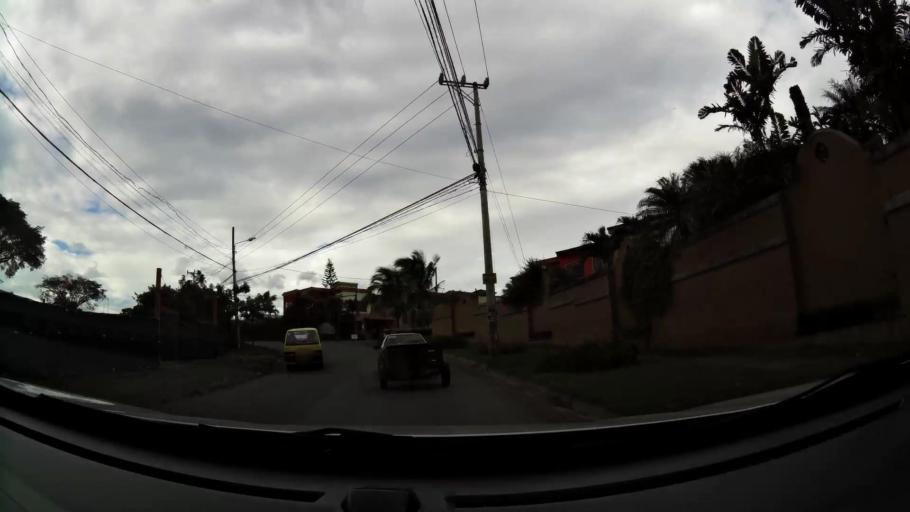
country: CR
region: Heredia
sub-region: Canton de Belen
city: San Antonio
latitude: 9.9629
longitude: -84.1952
